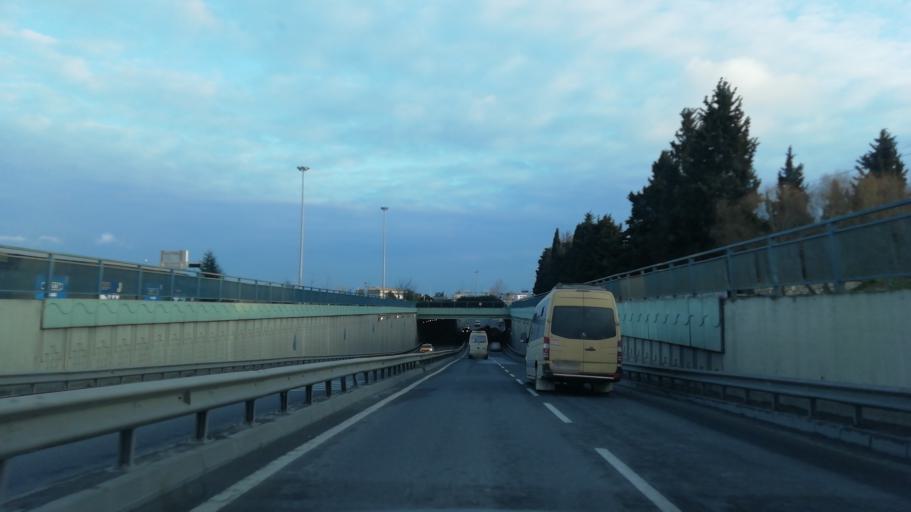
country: TR
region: Istanbul
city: Yakuplu
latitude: 40.9898
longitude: 28.7200
